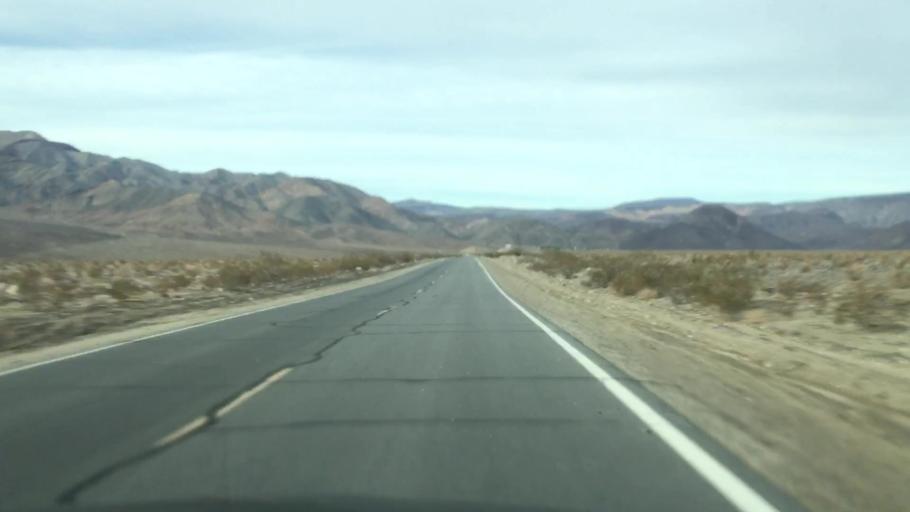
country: US
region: California
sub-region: San Bernardino County
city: Searles Valley
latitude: 36.3393
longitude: -117.4318
